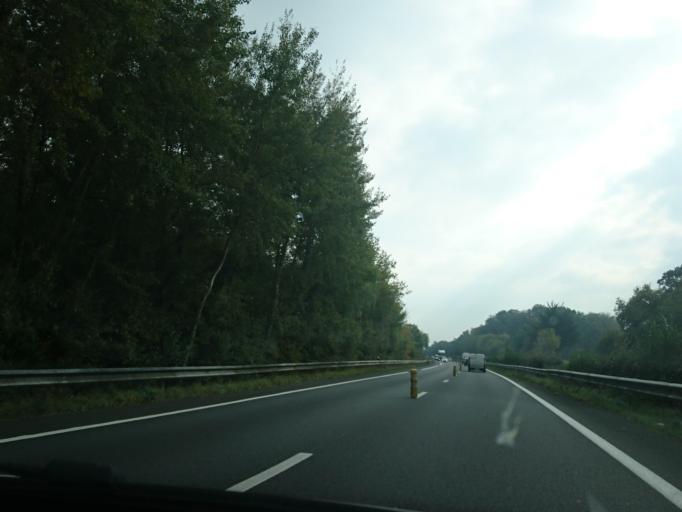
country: FR
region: Pays de la Loire
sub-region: Departement de la Loire-Atlantique
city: Nozay
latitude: 47.5633
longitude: -1.6348
